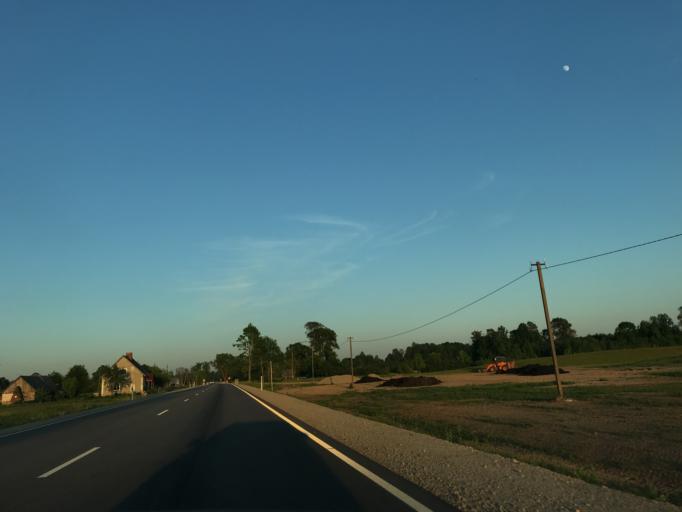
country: LV
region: Jaunjelgava
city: Jaunjelgava
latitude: 56.3991
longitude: 24.9425
